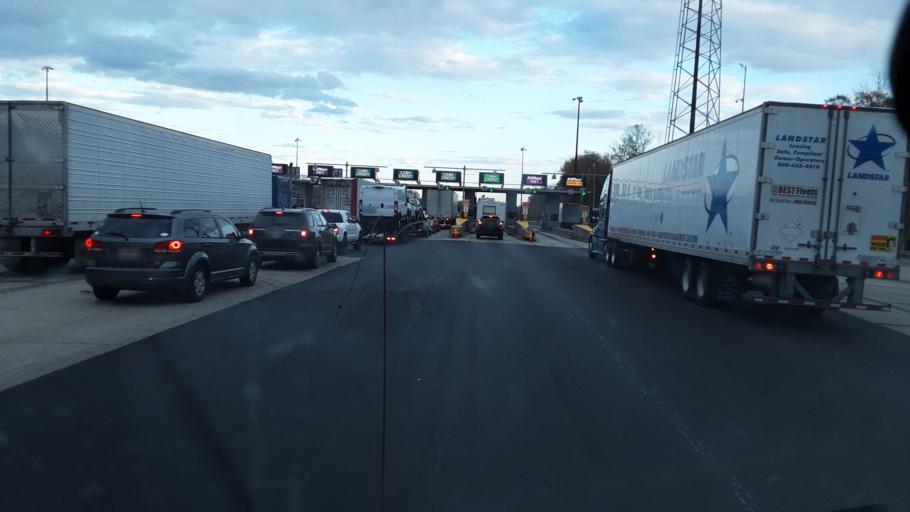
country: US
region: Indiana
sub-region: Steuben County
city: Fremont
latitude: 41.6663
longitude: -84.8544
